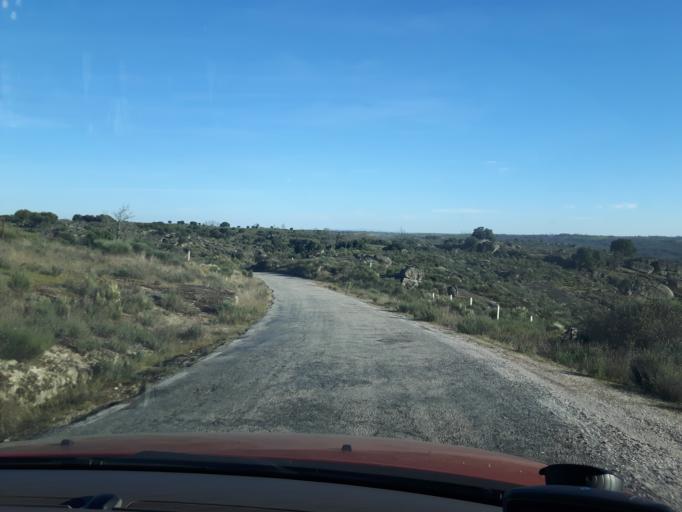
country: ES
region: Castille and Leon
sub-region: Provincia de Salamanca
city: Saldeana
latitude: 41.0105
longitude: -6.6268
